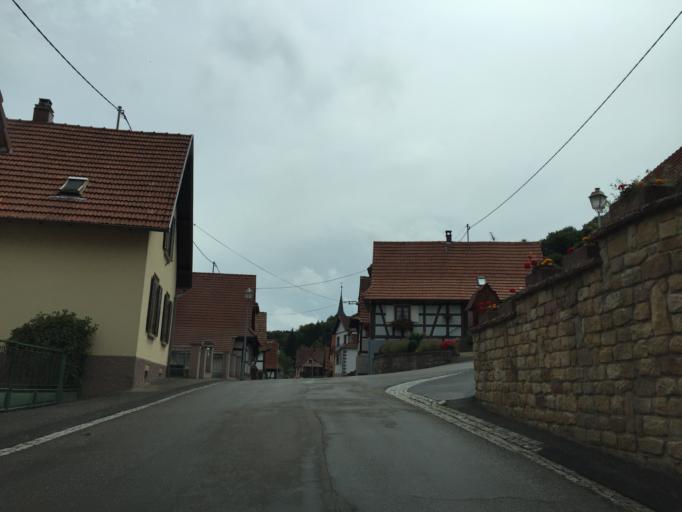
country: FR
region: Alsace
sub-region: Departement du Bas-Rhin
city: Soultz-sous-Forets
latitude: 48.9870
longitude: 7.8701
